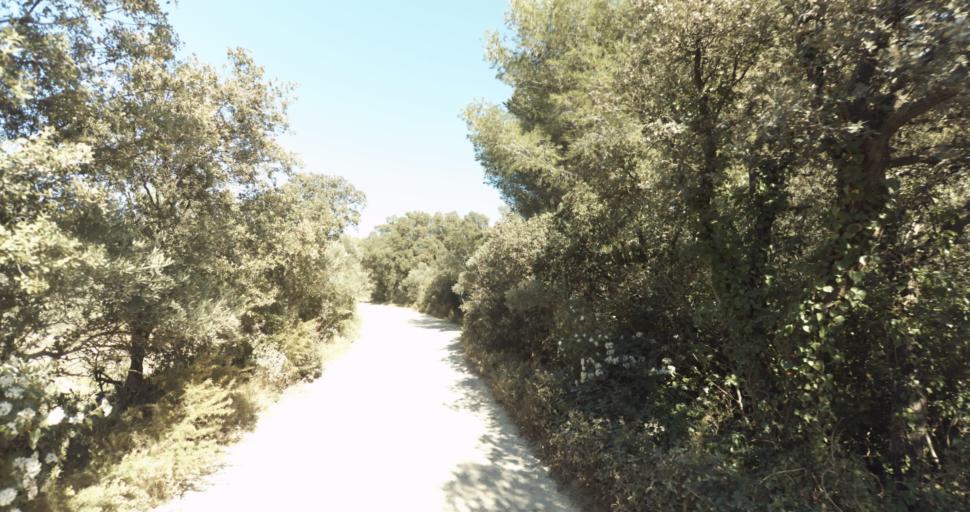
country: FR
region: Provence-Alpes-Cote d'Azur
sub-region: Departement des Bouches-du-Rhone
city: Pelissanne
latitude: 43.6473
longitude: 5.1710
